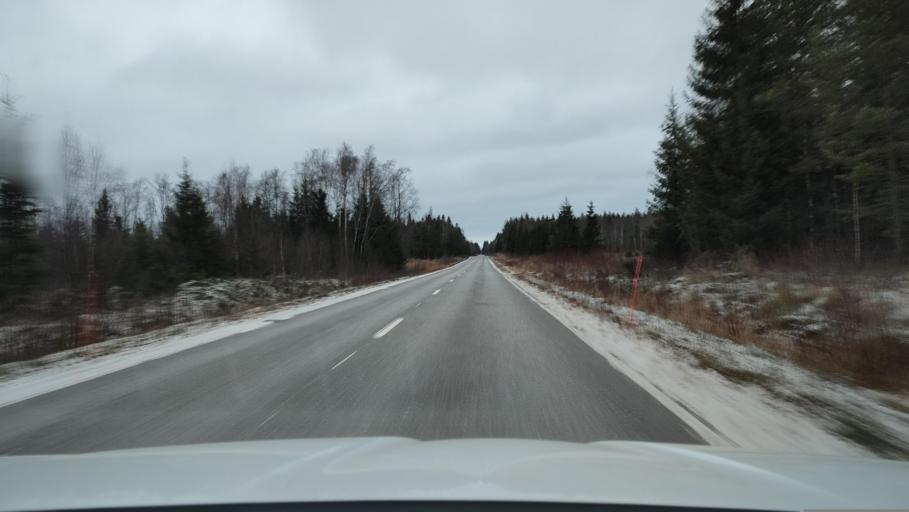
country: FI
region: Ostrobothnia
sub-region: Vaasa
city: Replot
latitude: 63.2571
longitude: 21.3666
